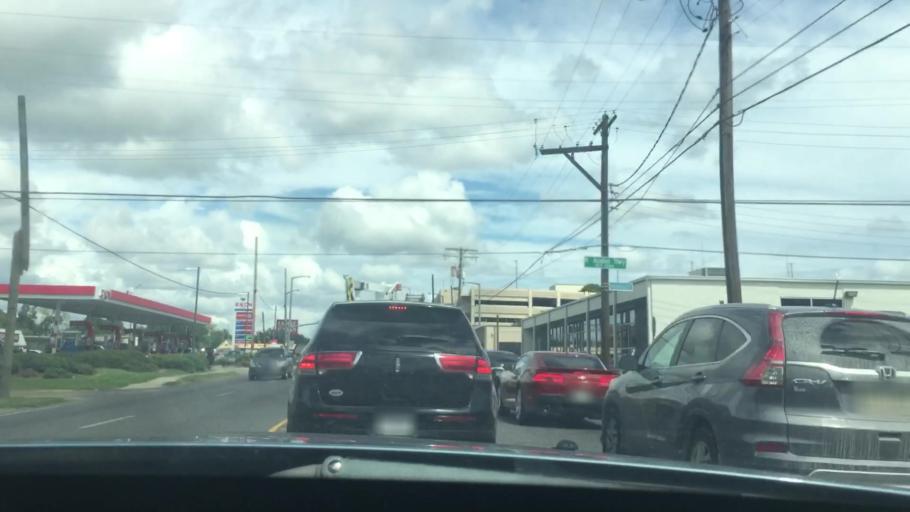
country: US
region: Louisiana
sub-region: East Baton Rouge Parish
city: Baton Rouge
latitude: 30.4503
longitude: -91.1566
